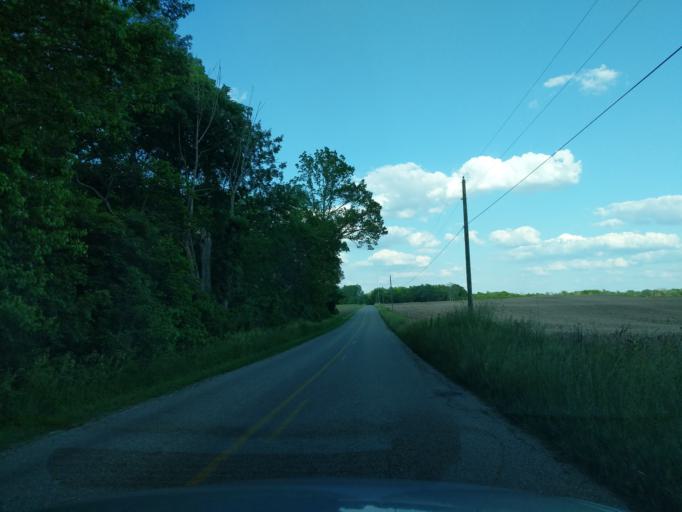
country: US
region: Indiana
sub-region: Whitley County
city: Tri-Lakes
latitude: 41.3026
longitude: -85.5616
